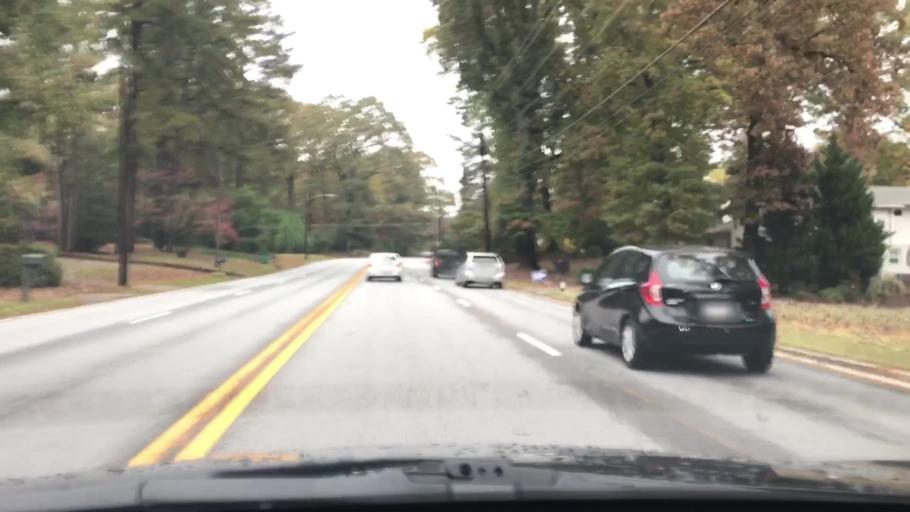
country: US
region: Georgia
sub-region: DeKalb County
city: North Druid Hills
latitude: 33.8170
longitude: -84.3056
